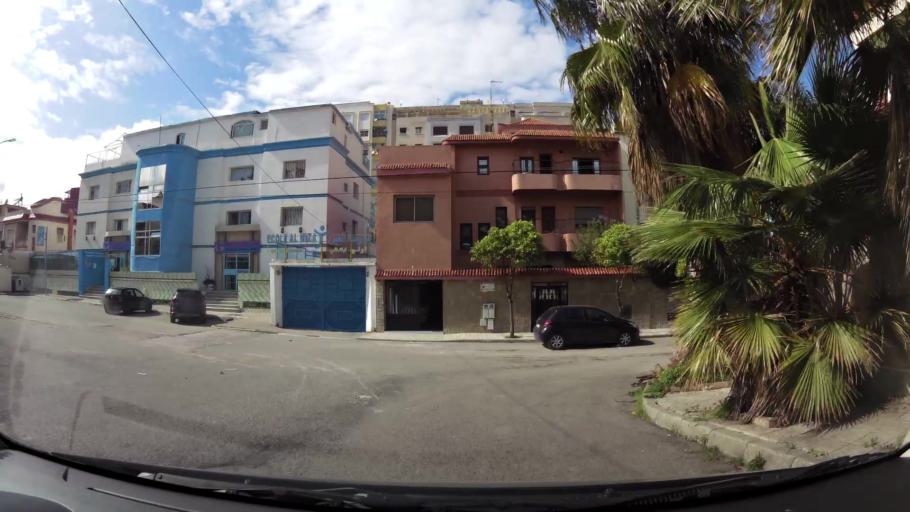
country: MA
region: Tanger-Tetouan
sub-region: Tanger-Assilah
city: Tangier
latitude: 35.7649
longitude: -5.8069
